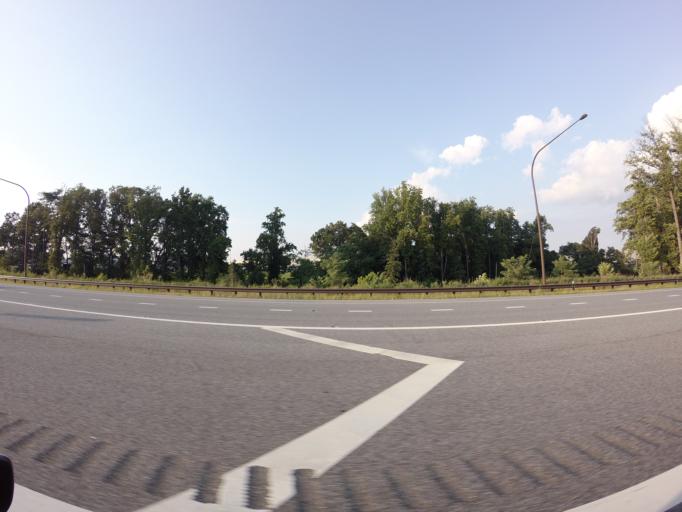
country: US
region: Maryland
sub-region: Montgomery County
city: Fairland
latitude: 39.0759
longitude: -76.9479
